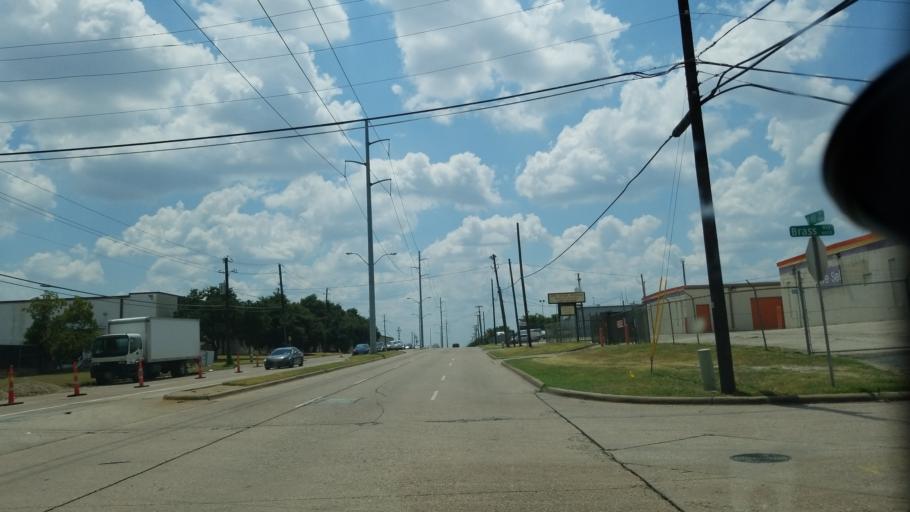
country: US
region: Texas
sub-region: Dallas County
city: Duncanville
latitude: 32.6846
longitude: -96.8916
